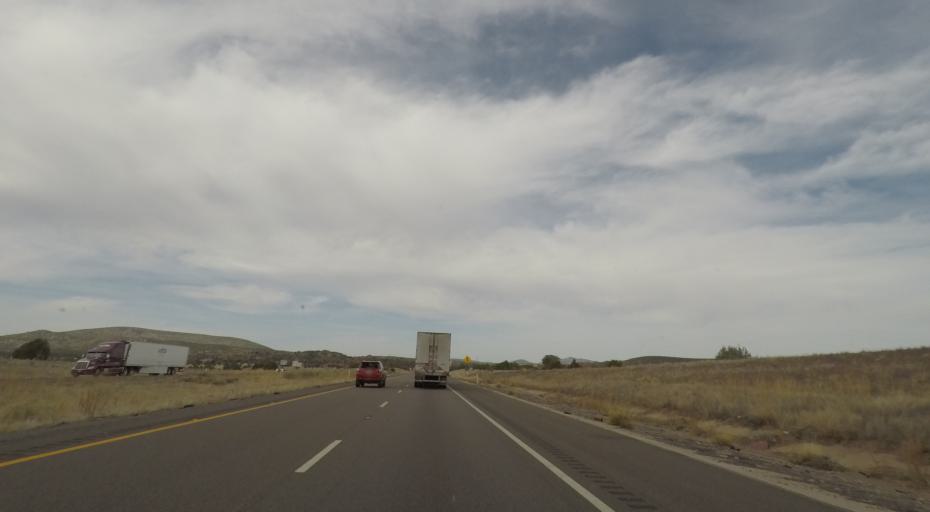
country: US
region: Arizona
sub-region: Mohave County
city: Peach Springs
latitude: 35.1910
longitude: -113.3661
